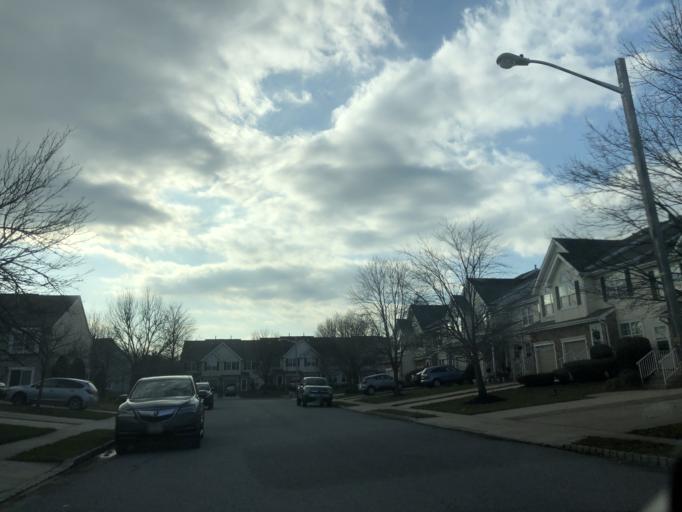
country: US
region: New Jersey
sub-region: Burlington County
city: Marlton
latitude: 39.9147
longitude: -74.9184
